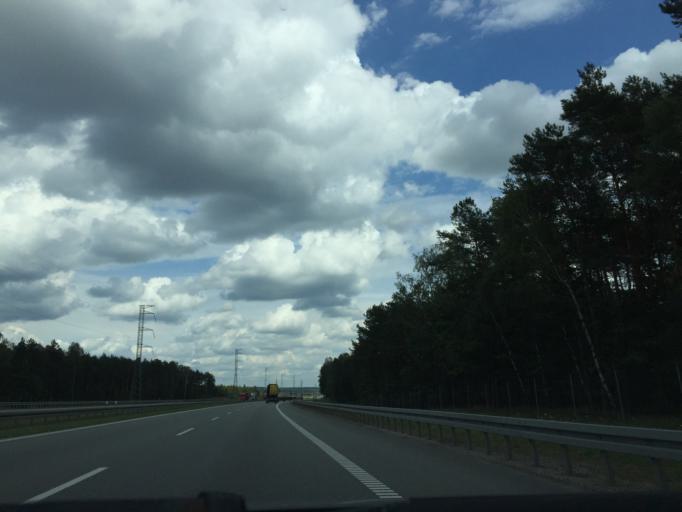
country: PL
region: Swietokrzyskie
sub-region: Powiat kielecki
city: Kostomloty Drugie
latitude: 50.9008
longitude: 20.5430
